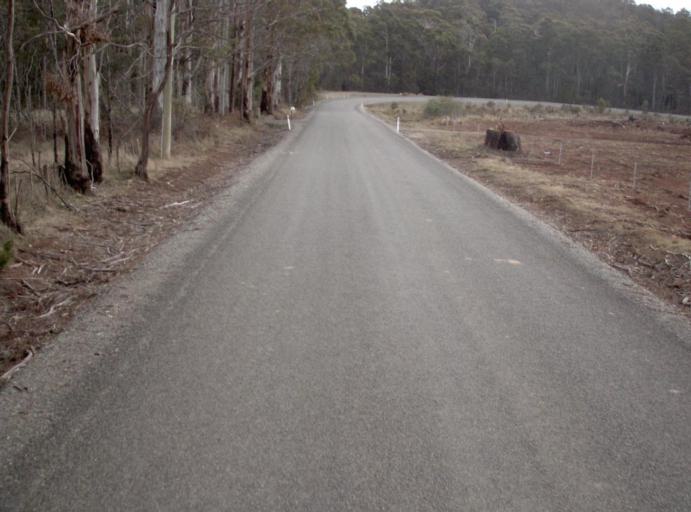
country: AU
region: Tasmania
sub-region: Launceston
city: Newstead
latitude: -41.3684
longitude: 147.2423
